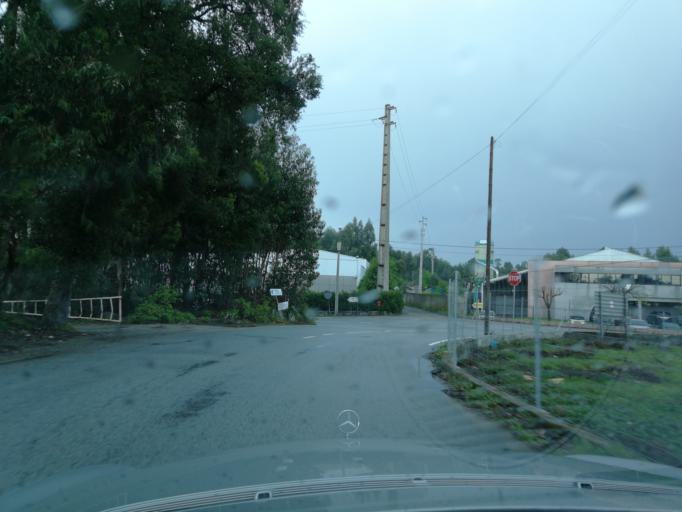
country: PT
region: Braga
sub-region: Vila Nova de Famalicao
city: Joane
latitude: 41.4658
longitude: -8.4280
